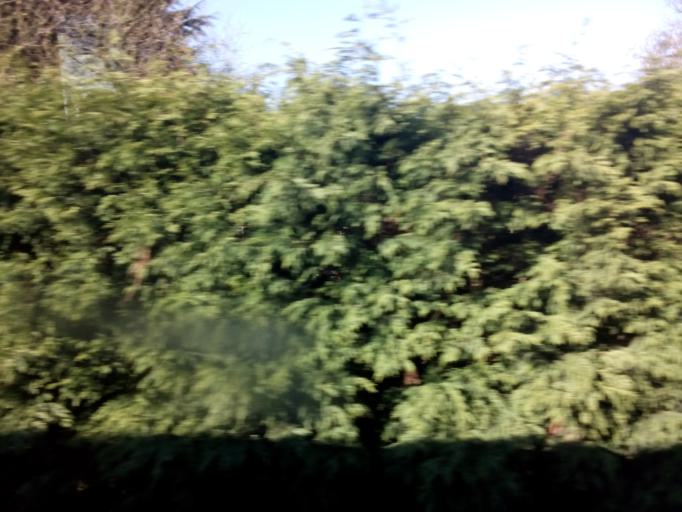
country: GB
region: England
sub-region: Northumberland
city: Morpeth
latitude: 55.1575
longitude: -1.6852
